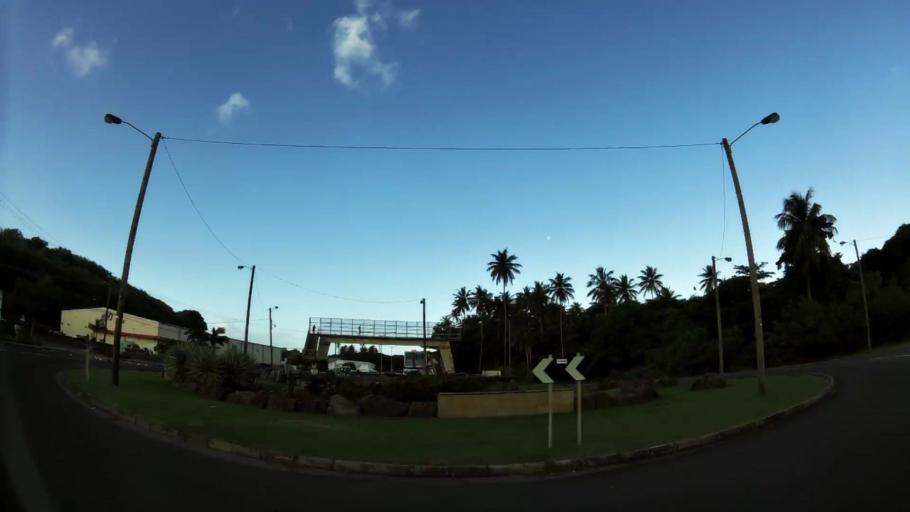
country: LC
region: Castries Quarter
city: Bisee
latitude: 14.0348
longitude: -60.9694
